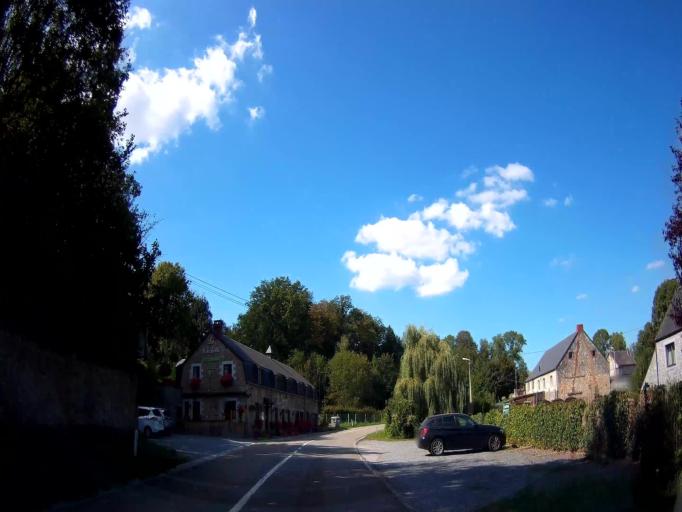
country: BE
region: Wallonia
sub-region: Province de Namur
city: Houyet
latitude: 50.2311
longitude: 5.0036
